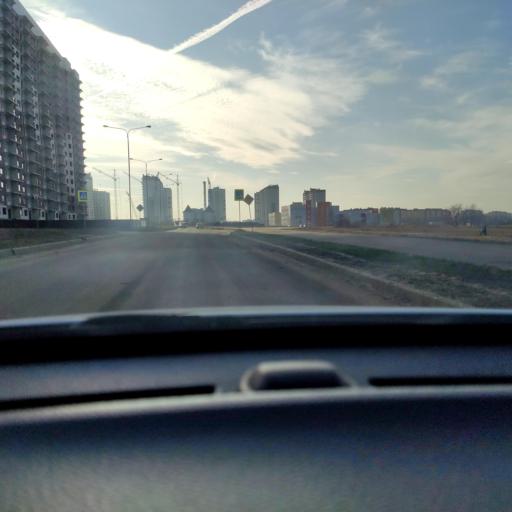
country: RU
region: Voronezj
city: Shilovo
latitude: 51.5718
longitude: 39.1212
